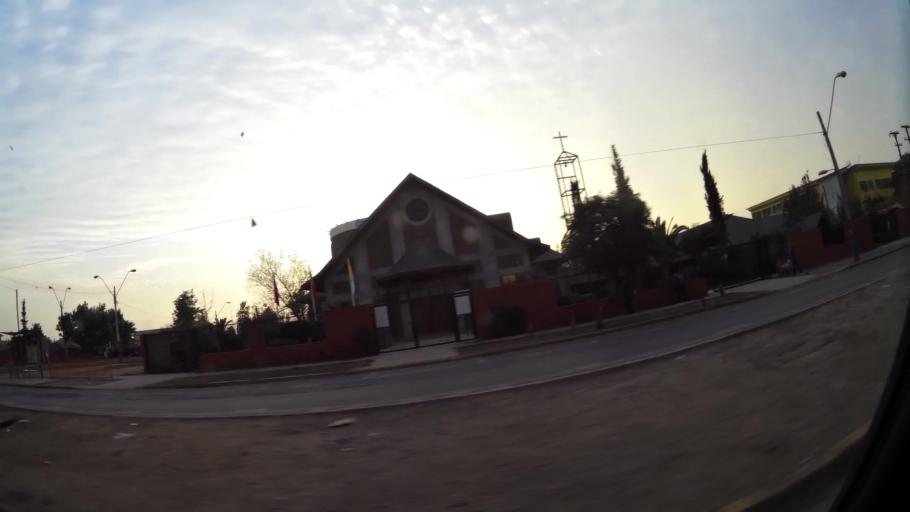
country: CL
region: Santiago Metropolitan
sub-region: Provincia de Santiago
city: Lo Prado
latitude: -33.5125
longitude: -70.7849
